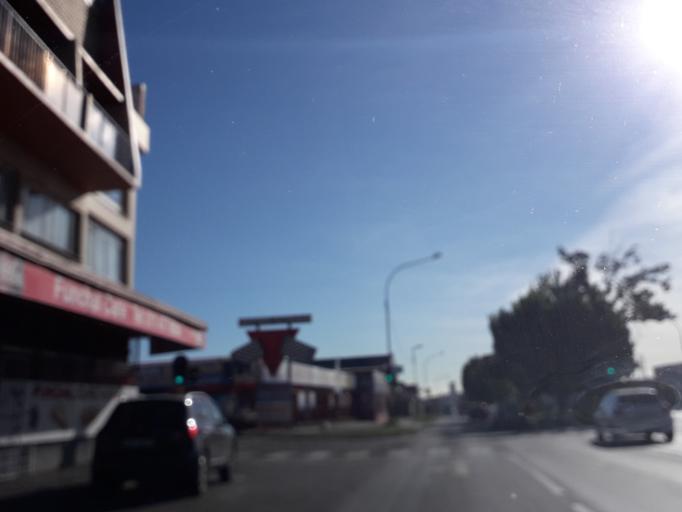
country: ZA
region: Gauteng
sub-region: City of Johannesburg Metropolitan Municipality
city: Roodepoort
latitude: -26.1747
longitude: 27.9527
